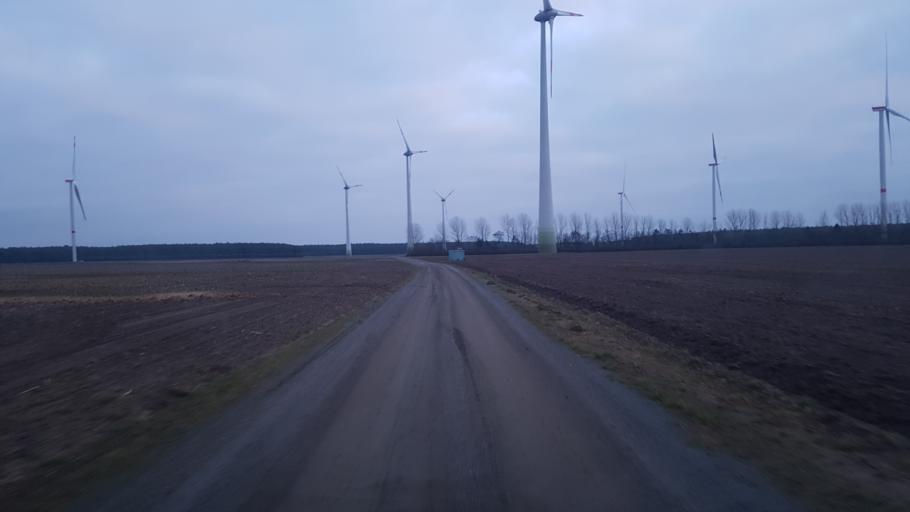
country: DE
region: Saxony-Anhalt
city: Holzdorf
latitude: 51.8578
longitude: 13.1259
